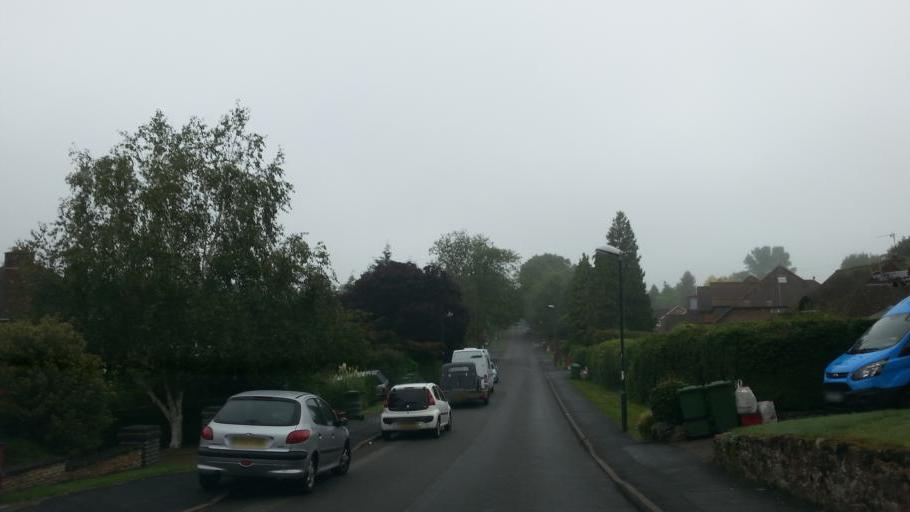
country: GB
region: England
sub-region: Warwickshire
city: Kenilworth
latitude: 52.3501
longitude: -1.5875
